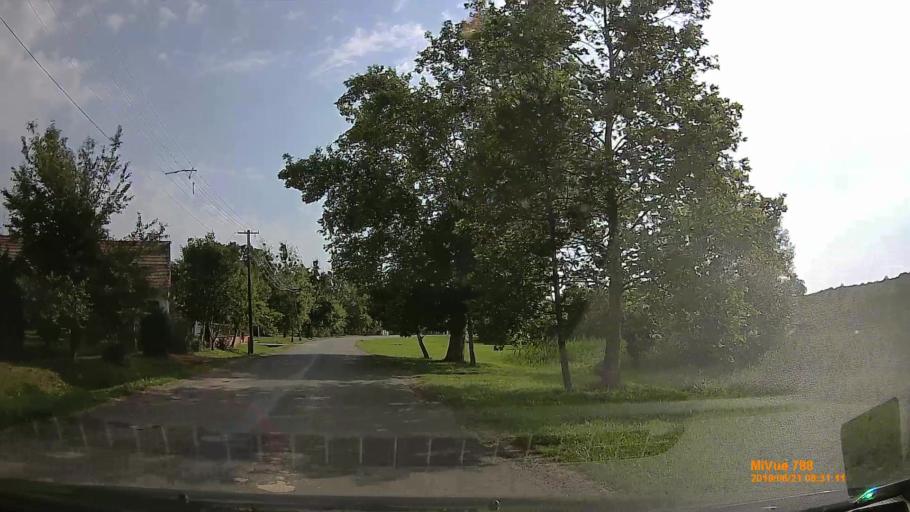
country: HU
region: Baranya
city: Szigetvar
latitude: 46.1516
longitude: 17.8658
